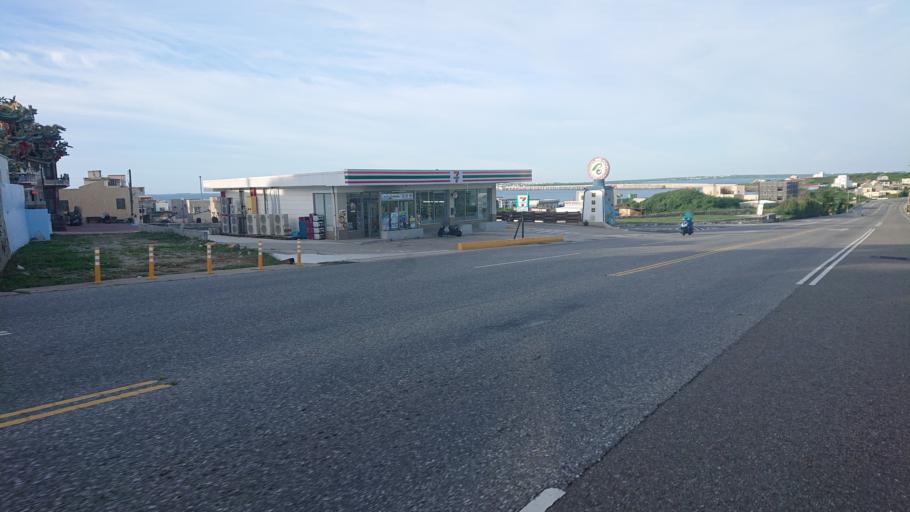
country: TW
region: Taiwan
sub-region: Penghu
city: Ma-kung
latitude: 23.6368
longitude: 119.5282
